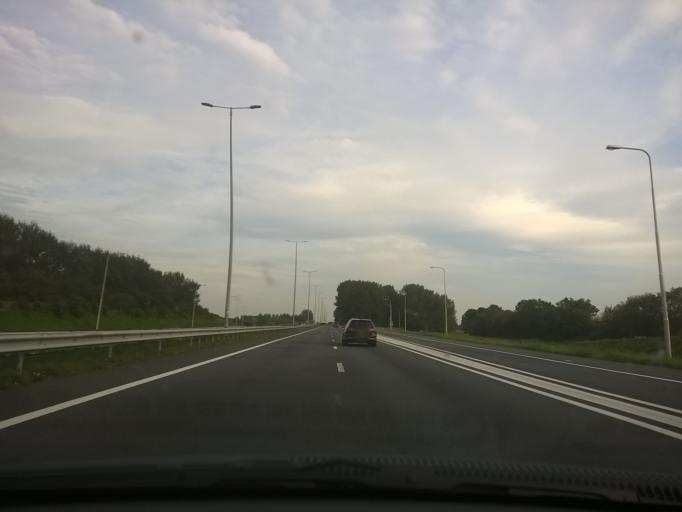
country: NL
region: Groningen
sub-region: Gemeente Groningen
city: Groningen
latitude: 53.2020
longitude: 6.5038
